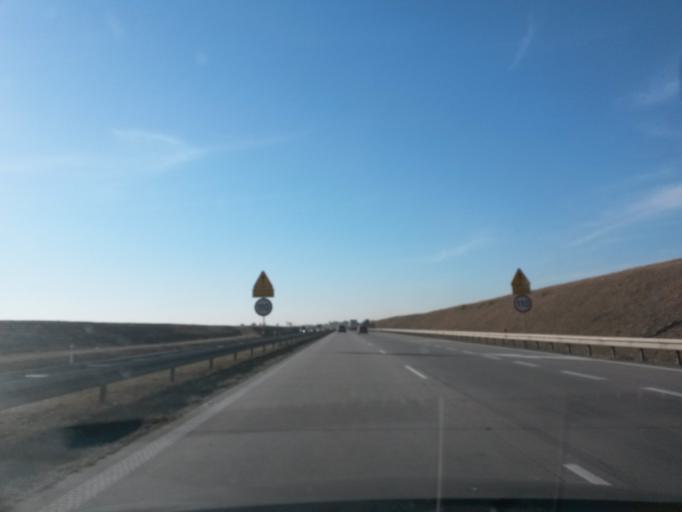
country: PL
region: Lower Silesian Voivodeship
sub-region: Powiat wroclawski
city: Katy Wroclawskie
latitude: 51.0307
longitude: 16.6463
